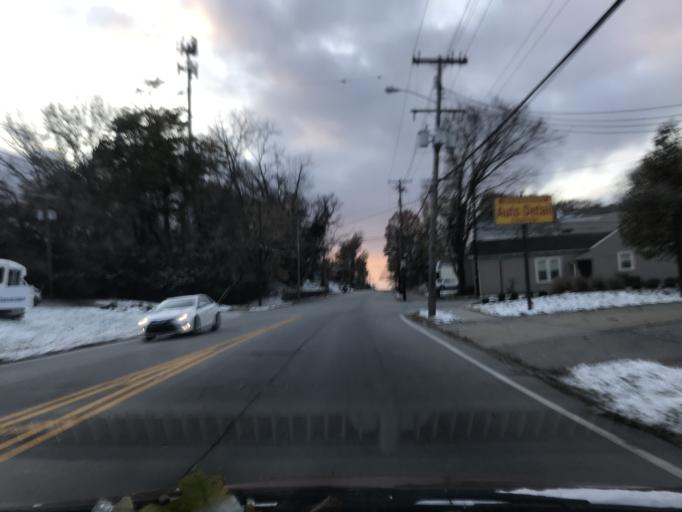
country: US
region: Indiana
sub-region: Clark County
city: Jeffersonville
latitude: 38.2595
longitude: -85.7121
